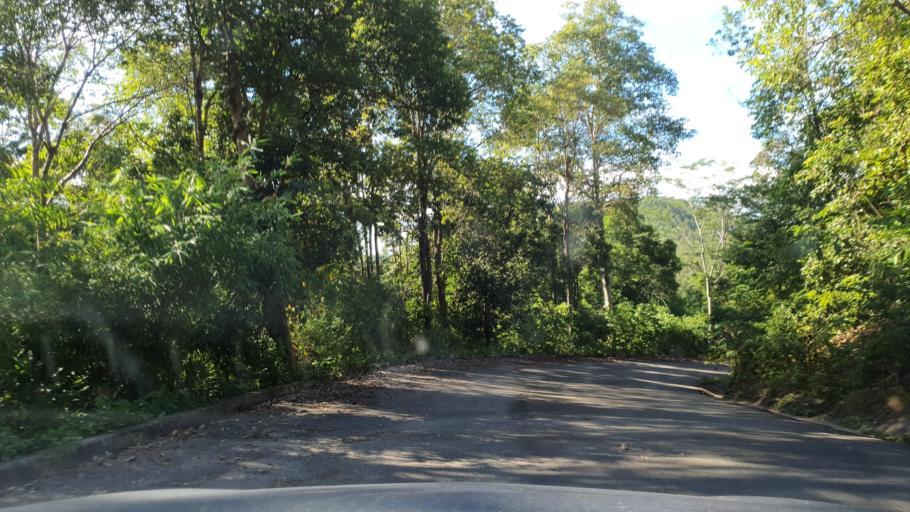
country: TH
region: Chiang Mai
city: Mae On
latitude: 18.7731
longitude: 99.2888
